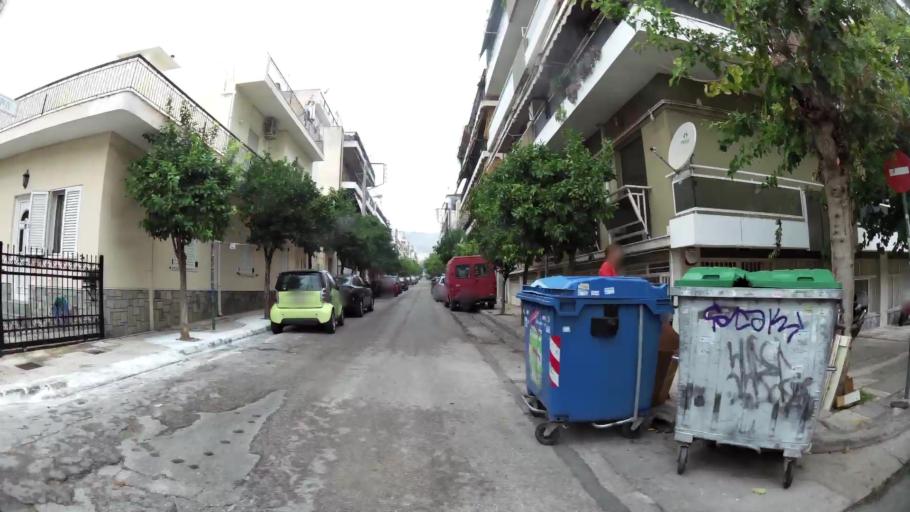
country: GR
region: Attica
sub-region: Nomarchia Athinas
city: Agia Varvara
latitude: 37.9837
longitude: 23.6602
